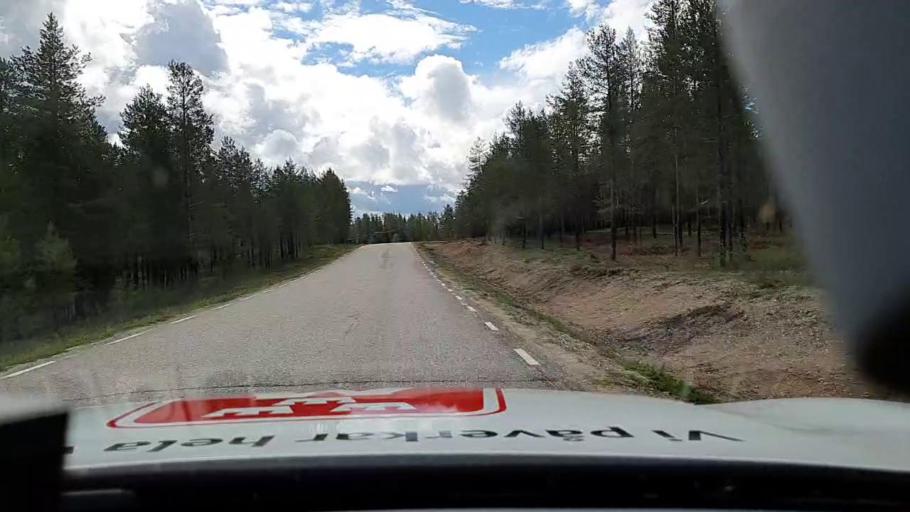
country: SE
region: Norrbotten
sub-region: Overkalix Kommun
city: OEverkalix
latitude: 66.2396
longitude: 22.9293
